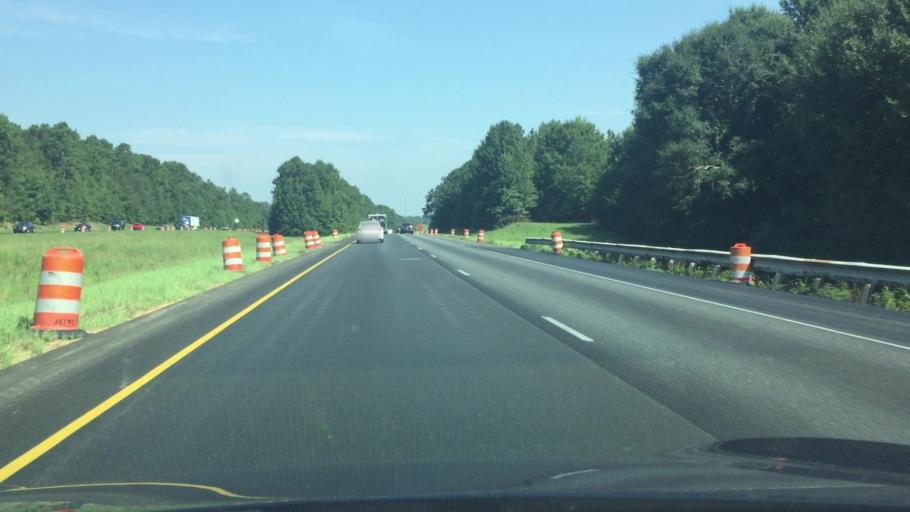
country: US
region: Alabama
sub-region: Chilton County
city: Clanton
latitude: 32.7680
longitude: -86.5642
